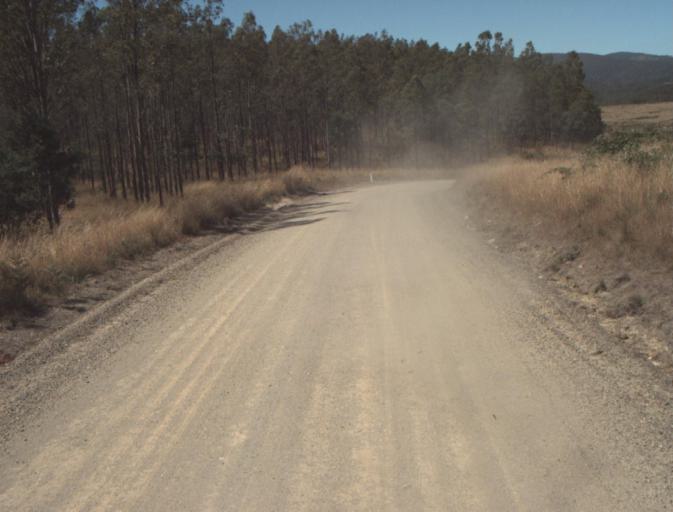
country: AU
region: Tasmania
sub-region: Dorset
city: Scottsdale
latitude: -41.3300
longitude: 147.4386
